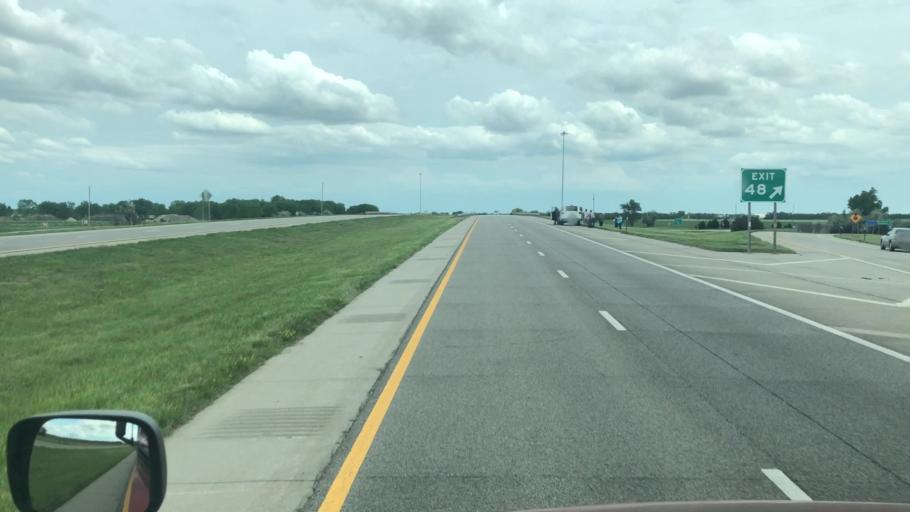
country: US
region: Kansas
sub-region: McPherson County
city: Moundridge
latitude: 38.2318
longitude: -97.5212
